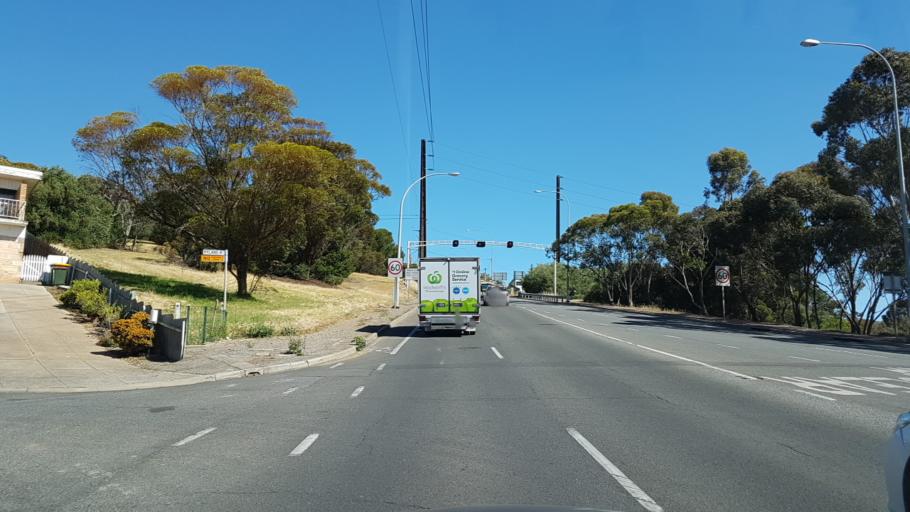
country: AU
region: South Australia
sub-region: Onkaparinga
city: Bedford Park
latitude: -35.0272
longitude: 138.5596
